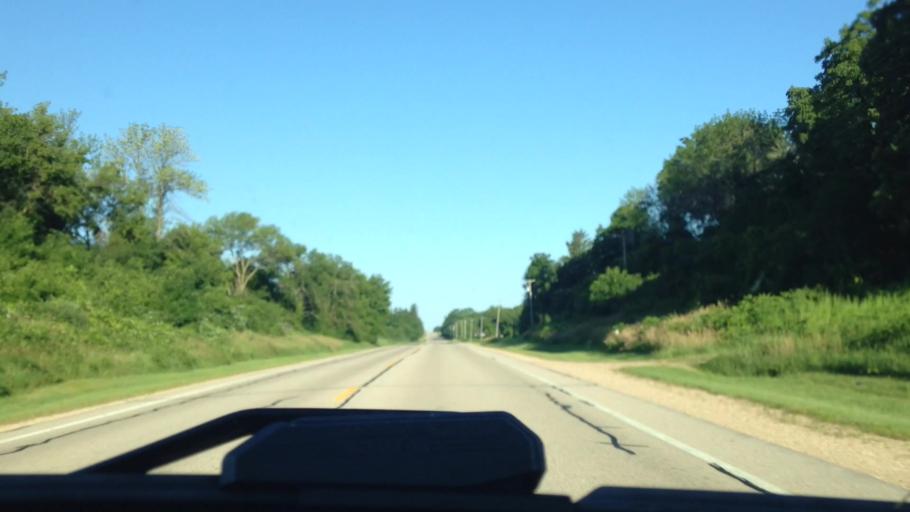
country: US
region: Wisconsin
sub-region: Dane County
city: De Forest
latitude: 43.3327
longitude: -89.2745
